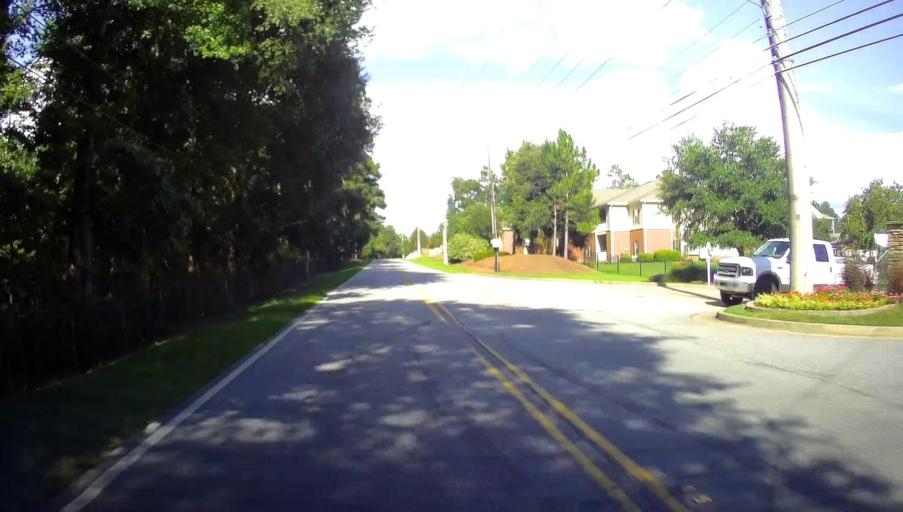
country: US
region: Georgia
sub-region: Muscogee County
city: Columbus
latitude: 32.5505
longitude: -84.8815
